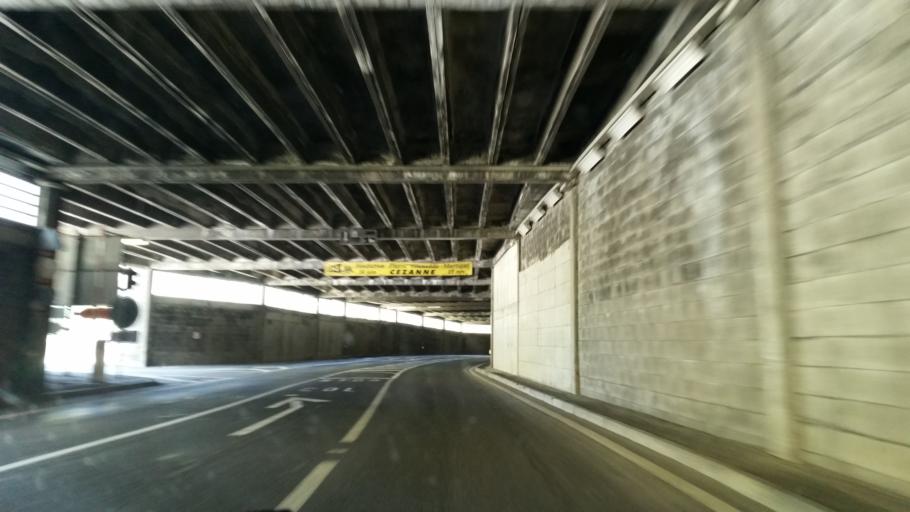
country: IT
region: Aosta Valley
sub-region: Valle d'Aosta
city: Saint-Oyen
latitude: 45.9026
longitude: 7.1972
